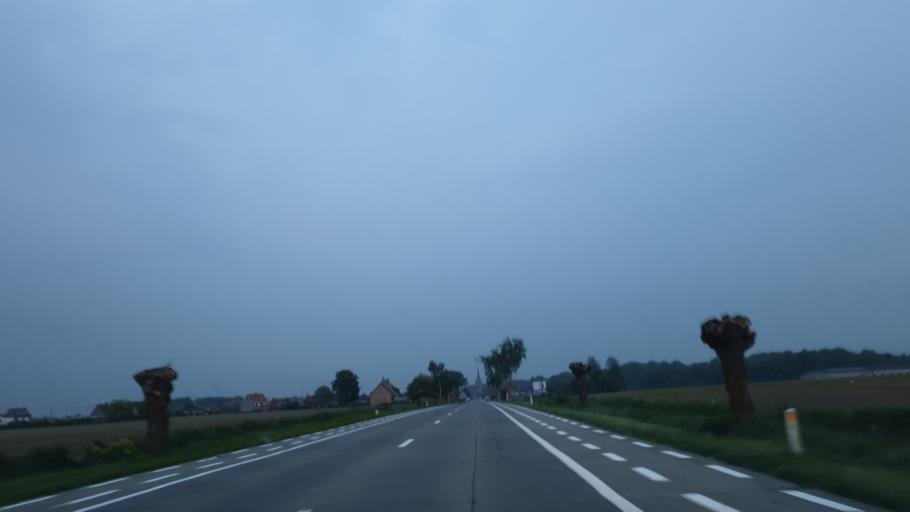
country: BE
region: Flanders
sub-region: Provincie West-Vlaanderen
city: Poperinge
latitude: 50.8922
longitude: 2.8038
